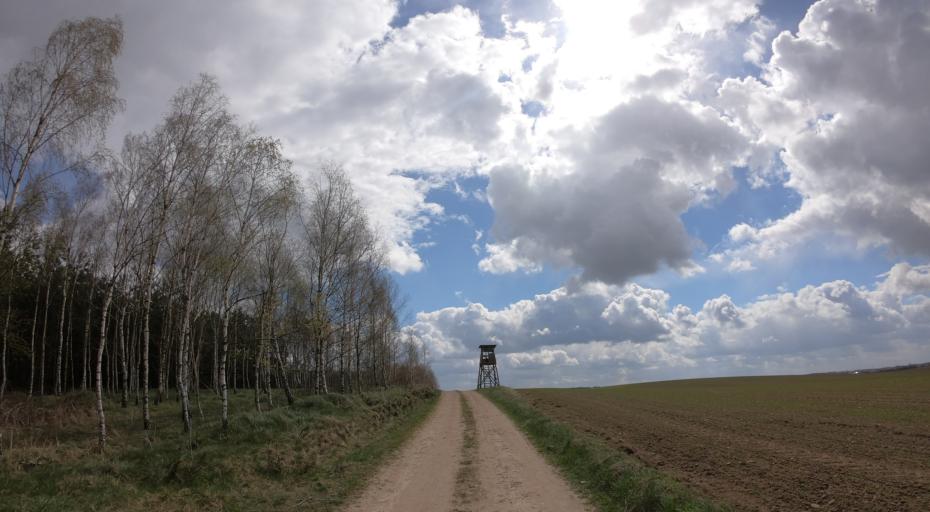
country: PL
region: West Pomeranian Voivodeship
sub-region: Powiat drawski
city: Drawsko Pomorskie
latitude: 53.5540
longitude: 15.8572
